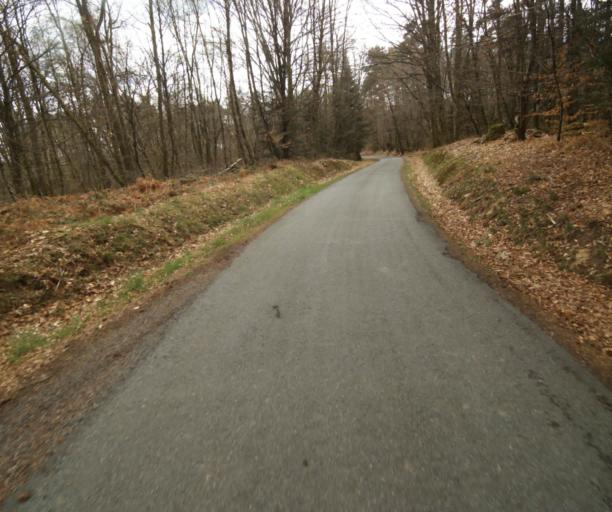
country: FR
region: Limousin
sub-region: Departement de la Correze
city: Argentat
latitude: 45.1917
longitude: 1.9293
